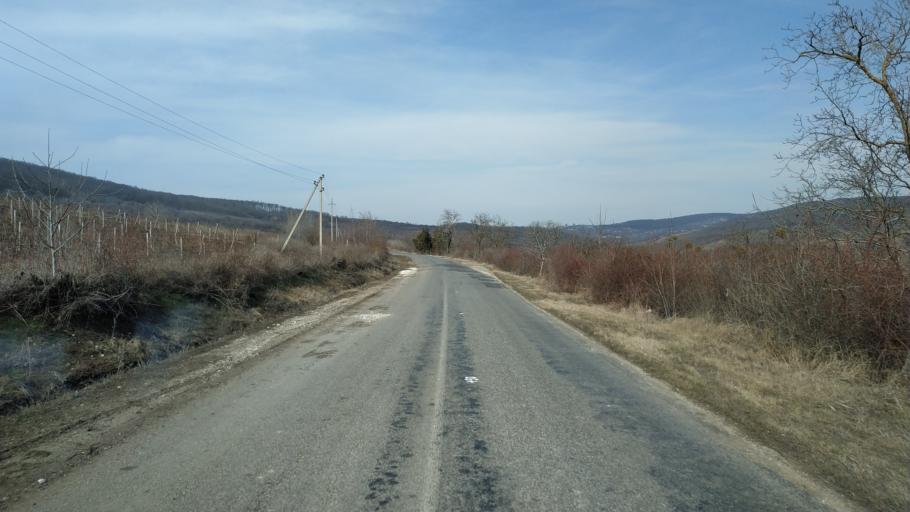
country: MD
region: Nisporeni
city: Nisporeni
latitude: 47.1763
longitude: 28.0854
